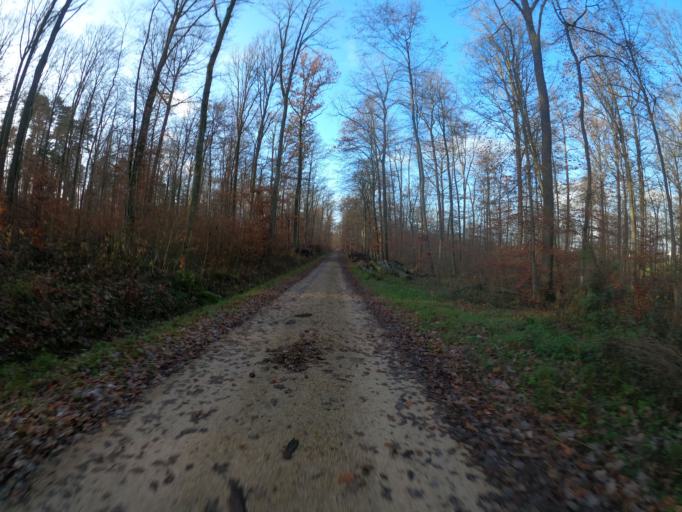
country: DE
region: Baden-Wuerttemberg
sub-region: Regierungsbezirk Stuttgart
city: Schlierbach
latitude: 48.6699
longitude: 9.5359
